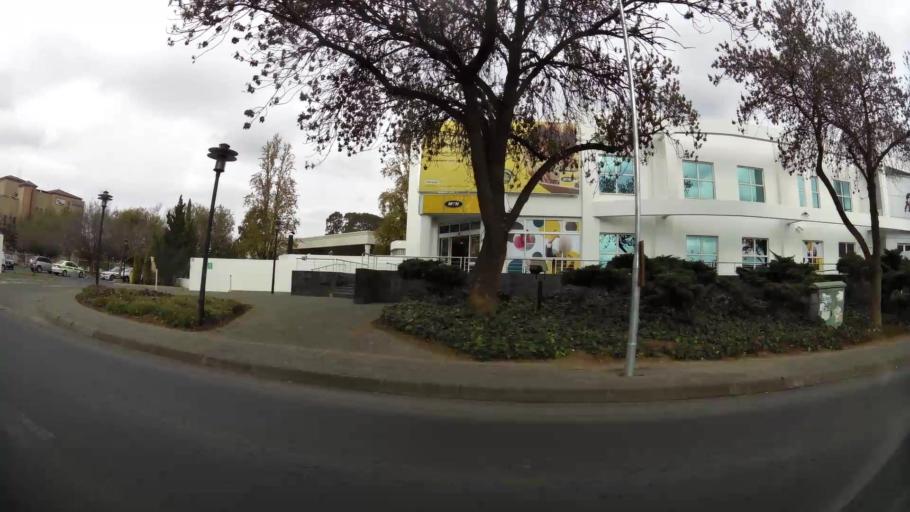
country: ZA
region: Orange Free State
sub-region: Mangaung Metropolitan Municipality
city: Bloemfontein
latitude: -29.1114
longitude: 26.2076
